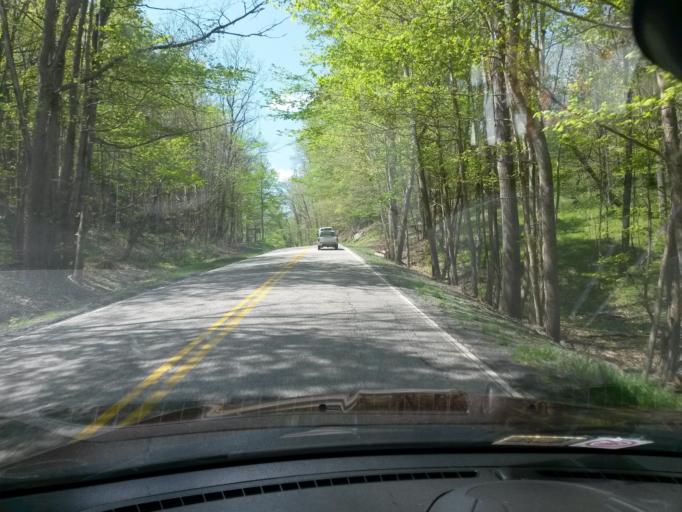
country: US
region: Virginia
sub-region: Bath County
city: Warm Springs
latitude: 37.9604
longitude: -79.8629
